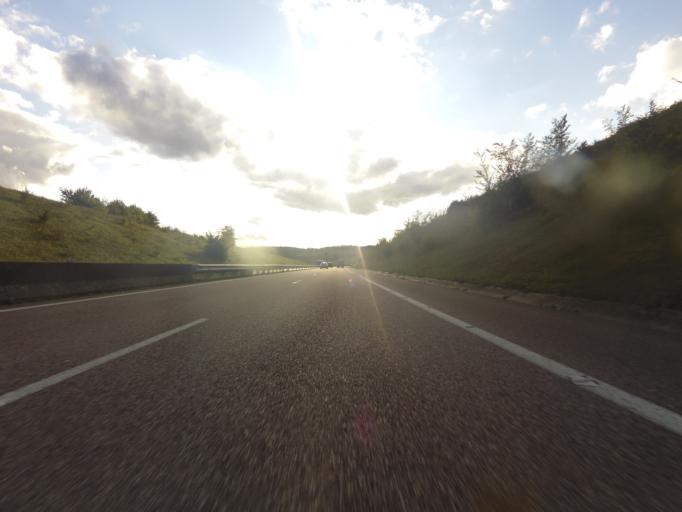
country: FR
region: Haute-Normandie
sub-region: Departement de la Seine-Maritime
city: Gaillefontaine
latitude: 49.7384
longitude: 1.5754
